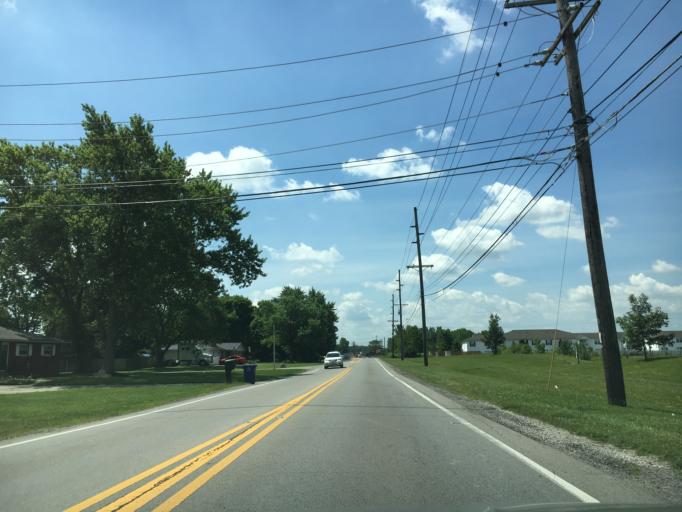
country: US
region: Ohio
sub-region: Franklin County
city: Lincoln Village
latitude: 39.9181
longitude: -83.1441
